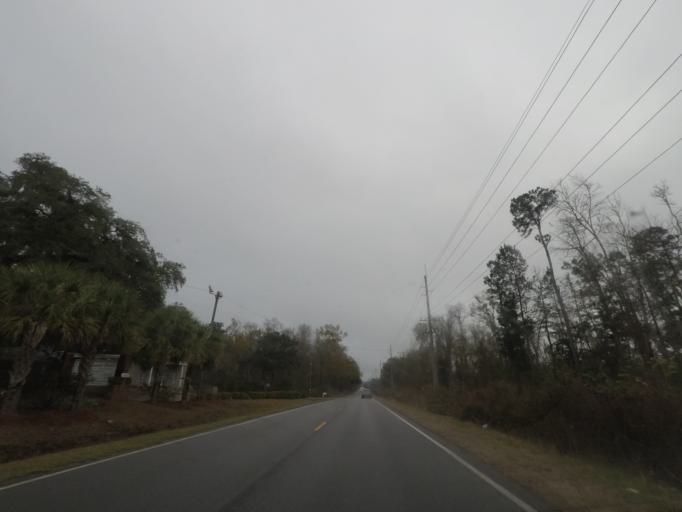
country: US
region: South Carolina
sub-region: Charleston County
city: Meggett
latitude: 32.6741
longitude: -80.3471
